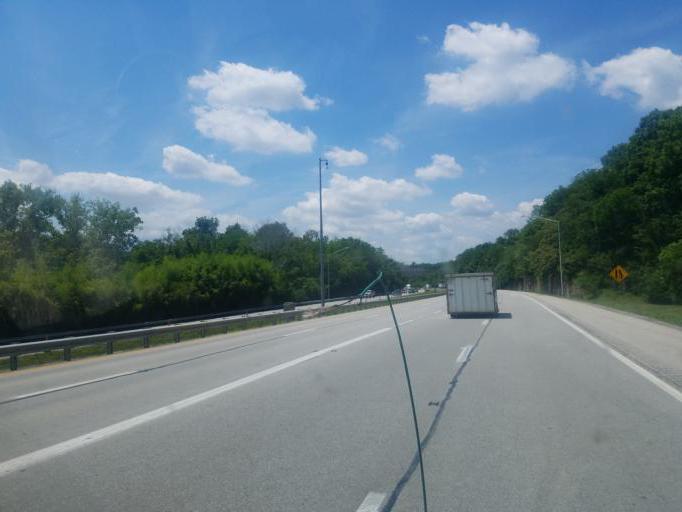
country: US
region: Kentucky
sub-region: Jefferson County
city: Northfield
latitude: 38.2915
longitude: -85.6499
